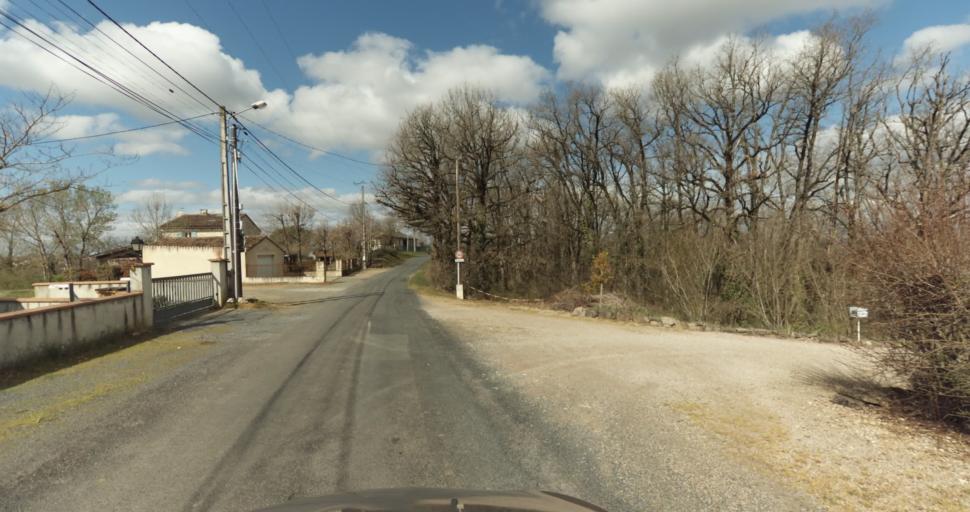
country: FR
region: Midi-Pyrenees
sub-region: Departement du Tarn
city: Puygouzon
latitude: 43.8829
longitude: 2.1524
